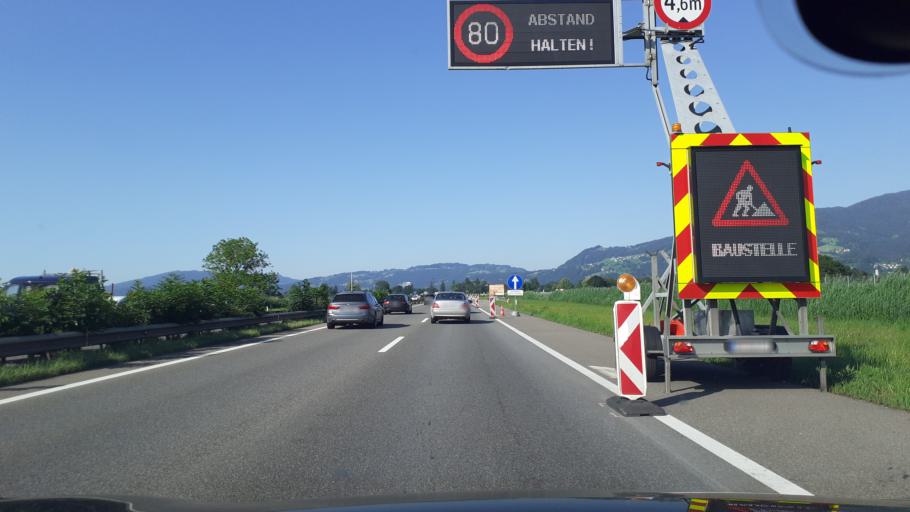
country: AT
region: Vorarlberg
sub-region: Politischer Bezirk Dornbirn
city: Hohenems
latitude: 47.3959
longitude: 9.6889
